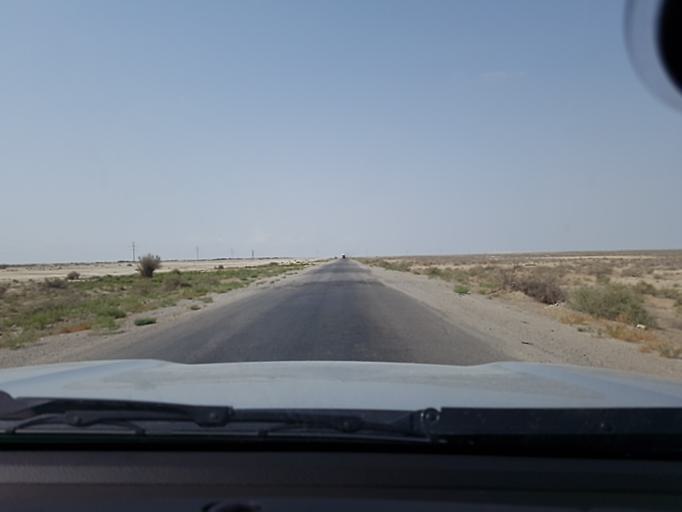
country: TM
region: Balkan
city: Gumdag
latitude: 38.7733
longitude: 54.5887
